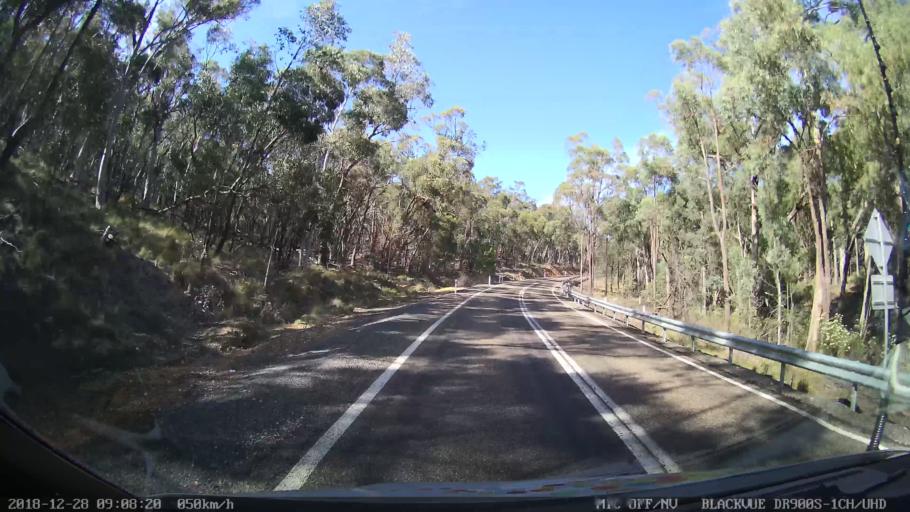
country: AU
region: New South Wales
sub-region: Upper Lachlan Shire
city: Crookwell
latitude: -34.2124
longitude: 149.3399
